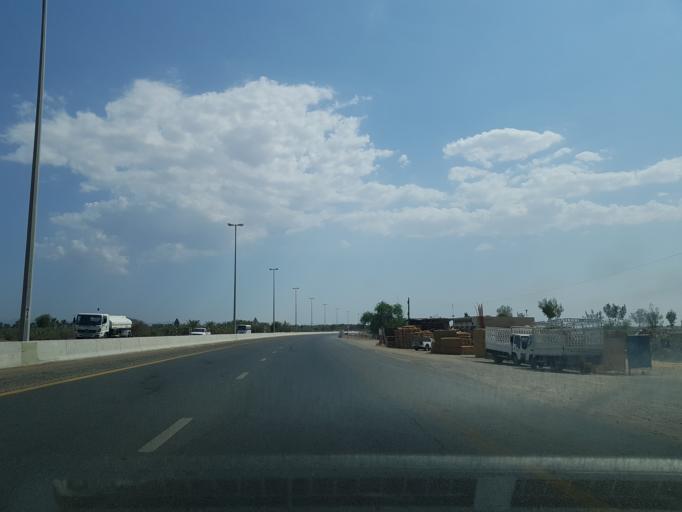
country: AE
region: Ash Shariqah
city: Adh Dhayd
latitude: 25.2415
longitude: 55.9148
